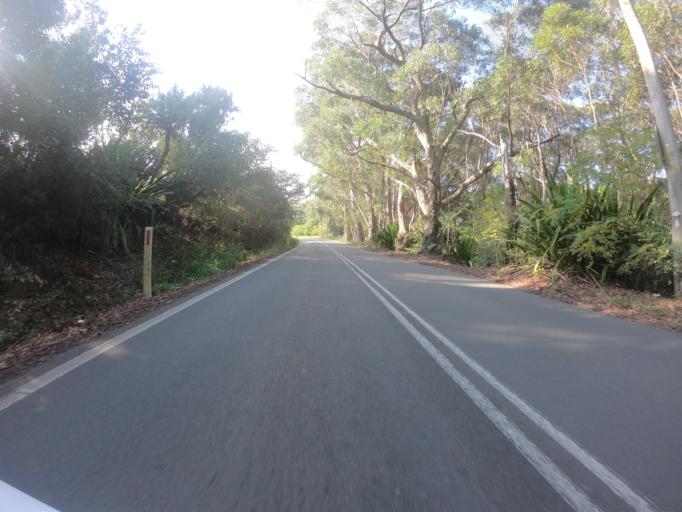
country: AU
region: New South Wales
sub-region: Wollongong
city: Helensburgh
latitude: -34.2119
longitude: 150.9770
